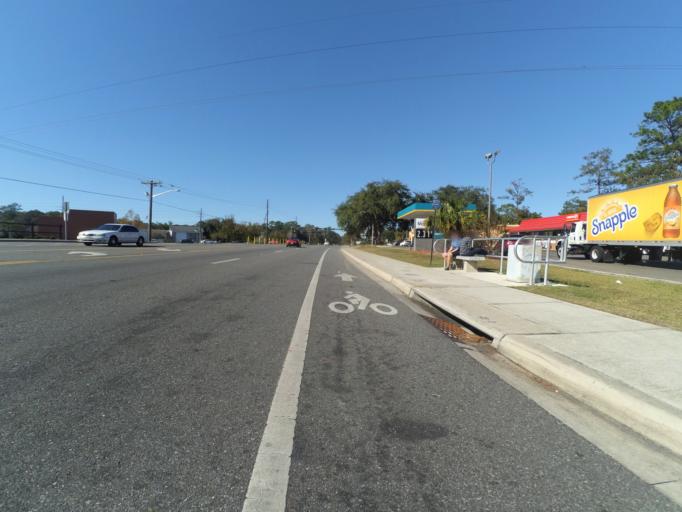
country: US
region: Florida
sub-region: Alachua County
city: Gainesville
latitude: 29.6356
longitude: -82.3879
